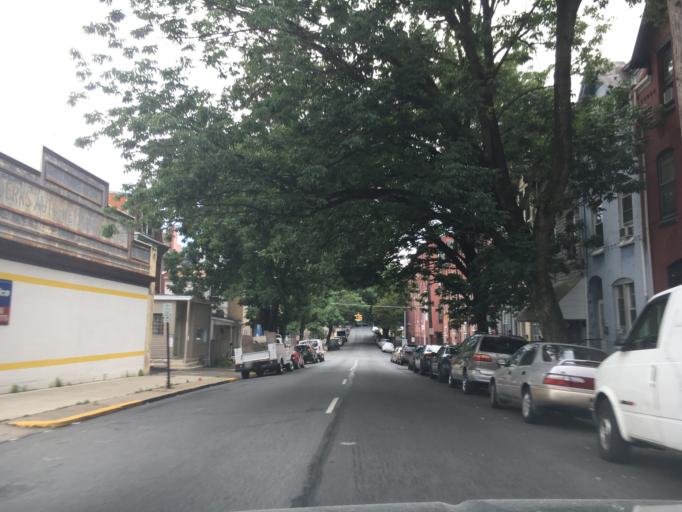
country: US
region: Pennsylvania
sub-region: Berks County
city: Reading
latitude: 40.3408
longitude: -75.9297
